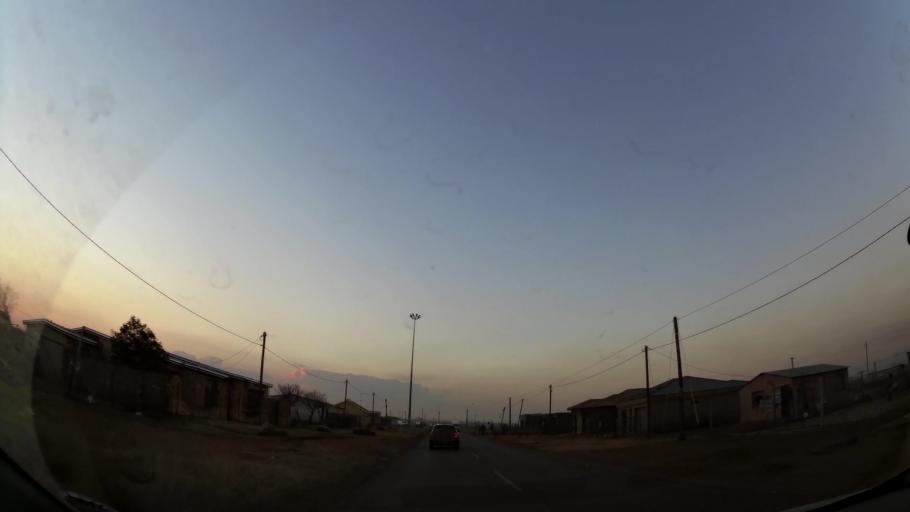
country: ZA
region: Gauteng
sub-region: Ekurhuleni Metropolitan Municipality
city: Nigel
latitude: -26.3615
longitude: 28.3928
